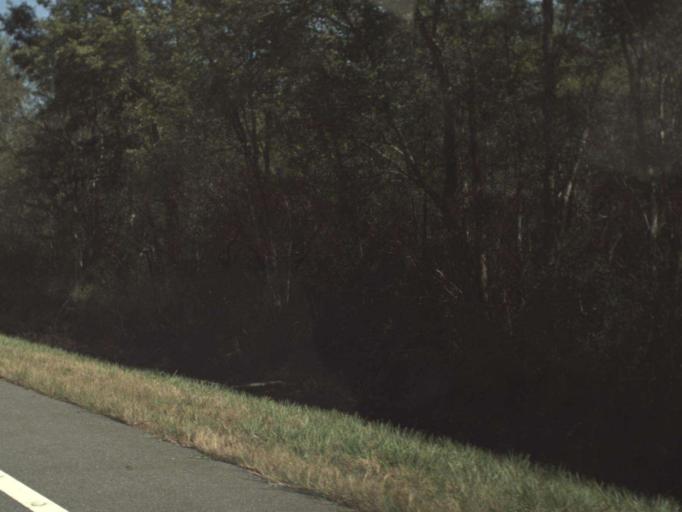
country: US
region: Florida
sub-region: Washington County
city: Chipley
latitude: 30.8249
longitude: -85.5331
